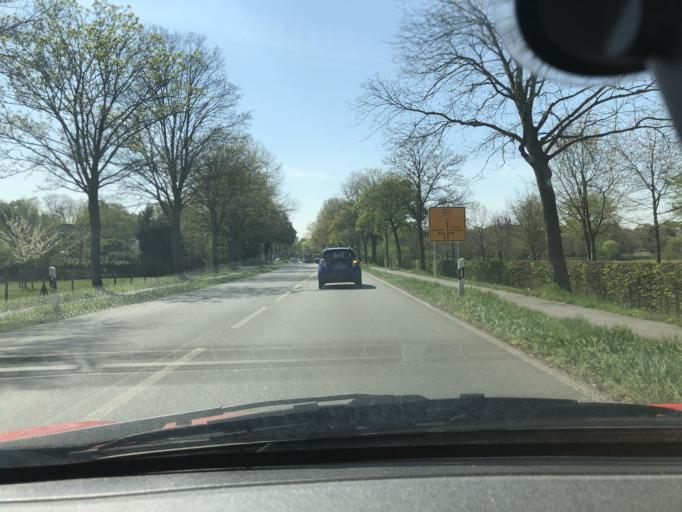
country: DE
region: North Rhine-Westphalia
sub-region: Regierungsbezirk Dusseldorf
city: Kamp-Lintfort
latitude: 51.5061
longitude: 6.5251
